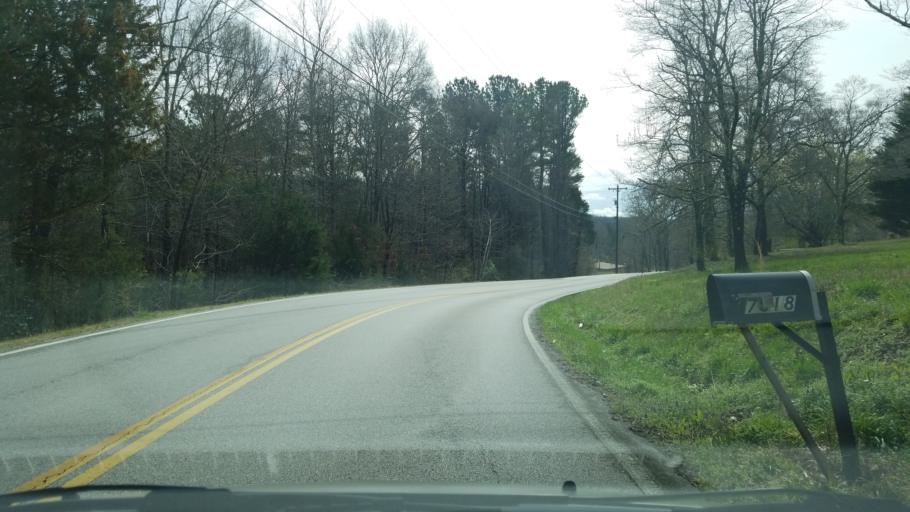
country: US
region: Tennessee
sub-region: Hamilton County
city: Harrison
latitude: 35.1373
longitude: -85.0854
